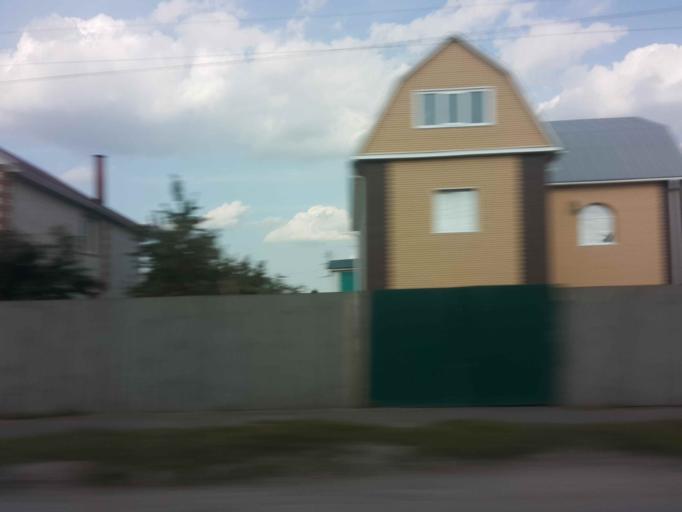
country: RU
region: Tambov
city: Tambov
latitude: 52.7158
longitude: 41.4392
